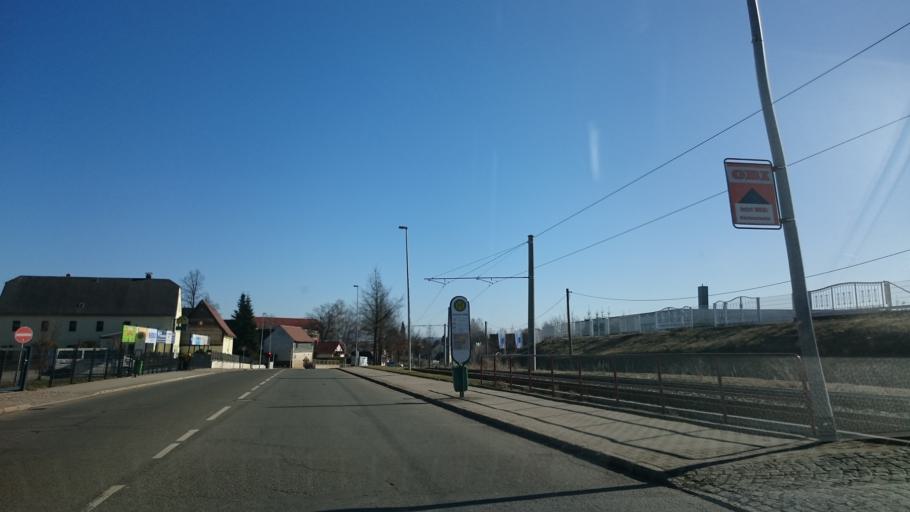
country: DE
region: Saxony
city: Lichtentanne
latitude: 50.7221
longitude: 12.4465
